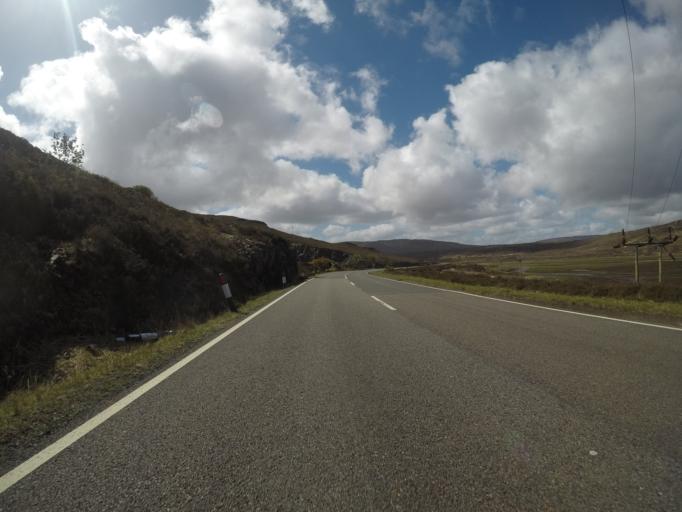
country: GB
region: Scotland
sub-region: Highland
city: Isle of Skye
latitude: 57.2969
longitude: -6.1555
